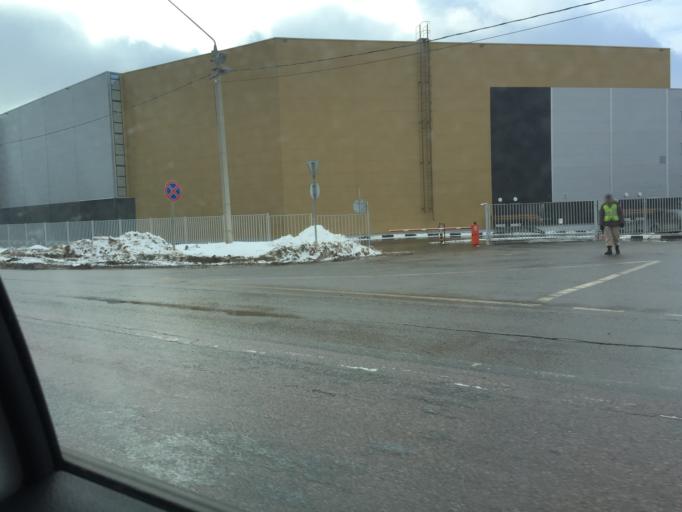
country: RU
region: Moskovskaya
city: Pavlovskaya Sloboda
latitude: 55.8170
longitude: 37.1144
